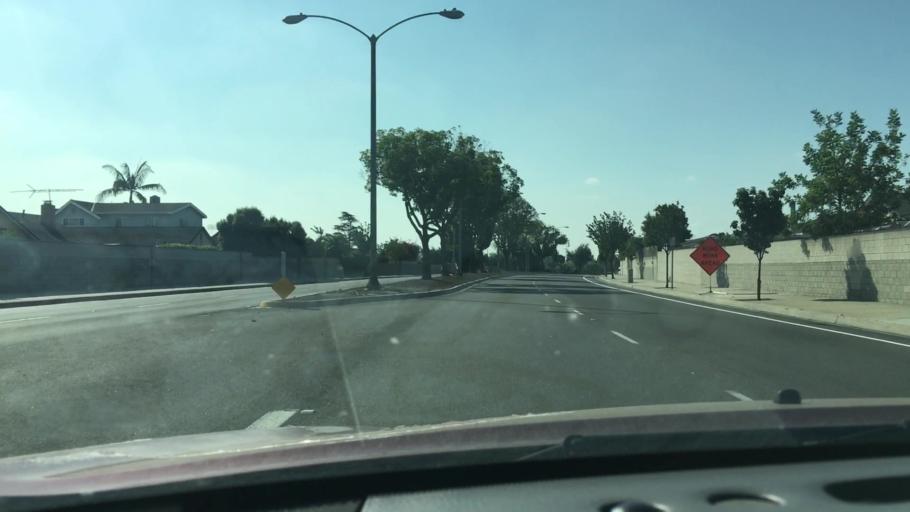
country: US
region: California
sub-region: Orange County
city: Buena Park
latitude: 33.8904
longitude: -118.0013
